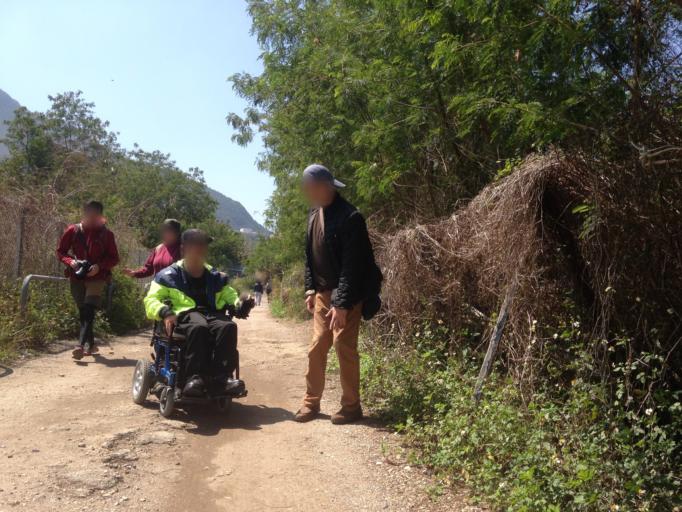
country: HK
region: Sai Kung
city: Sai Kung
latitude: 22.4325
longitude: 114.2547
